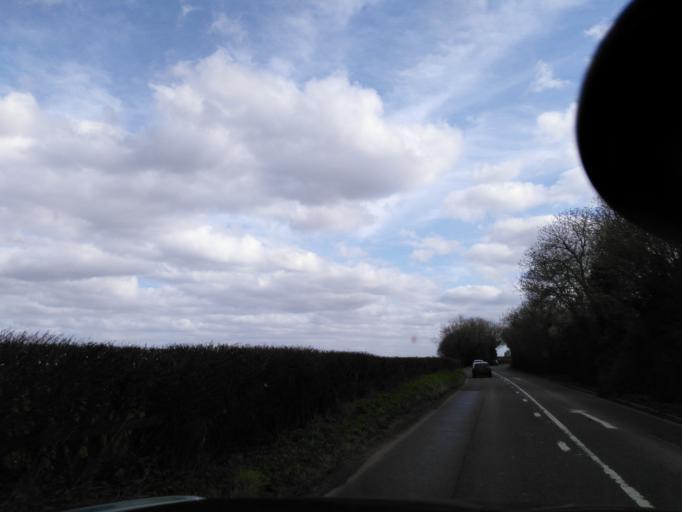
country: GB
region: England
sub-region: Wiltshire
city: Norton
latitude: 51.5313
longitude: -2.1253
